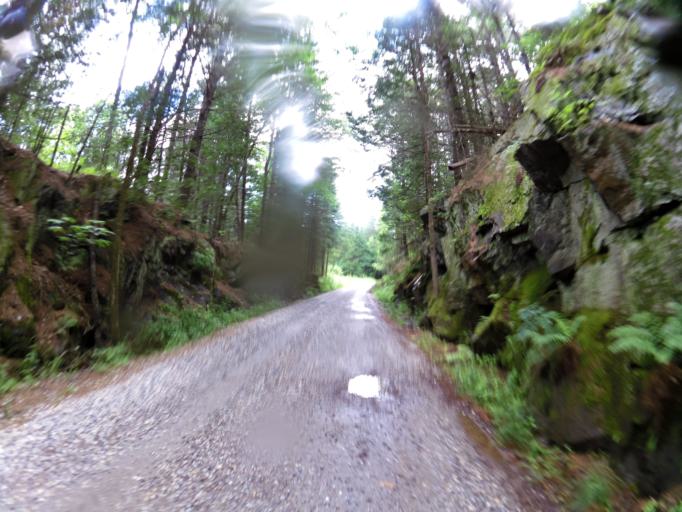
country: CA
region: Ontario
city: Renfrew
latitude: 45.0815
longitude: -76.7209
